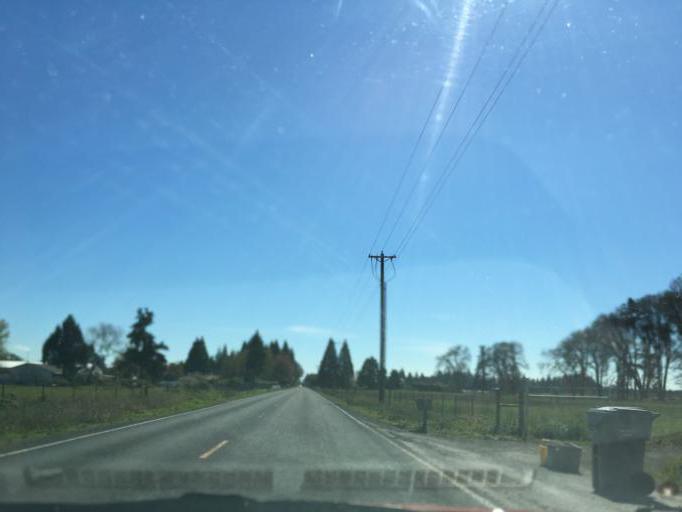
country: US
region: Oregon
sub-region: Clackamas County
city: Canby
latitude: 45.2126
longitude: -122.7228
